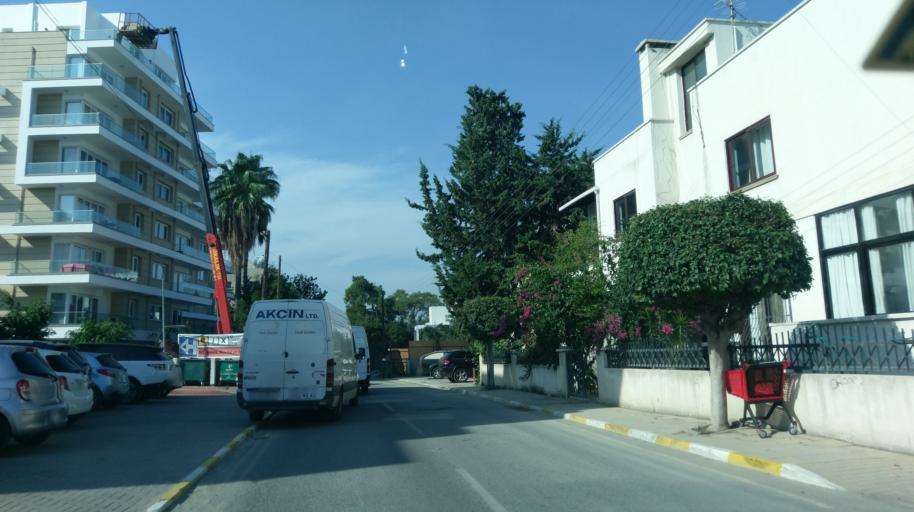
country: CY
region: Keryneia
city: Kyrenia
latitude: 35.3372
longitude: 33.3050
